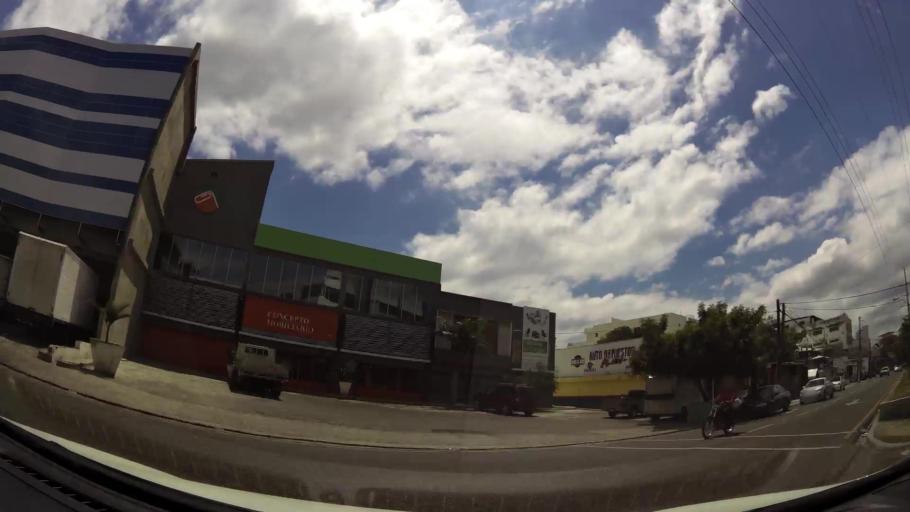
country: DO
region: Nacional
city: Bella Vista
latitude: 18.4333
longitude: -69.9606
